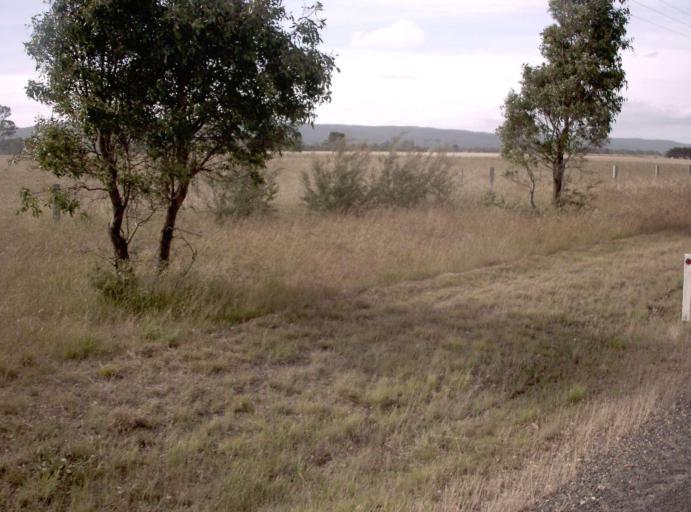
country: AU
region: Victoria
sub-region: Wellington
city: Heyfield
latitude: -38.0565
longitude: 146.6626
